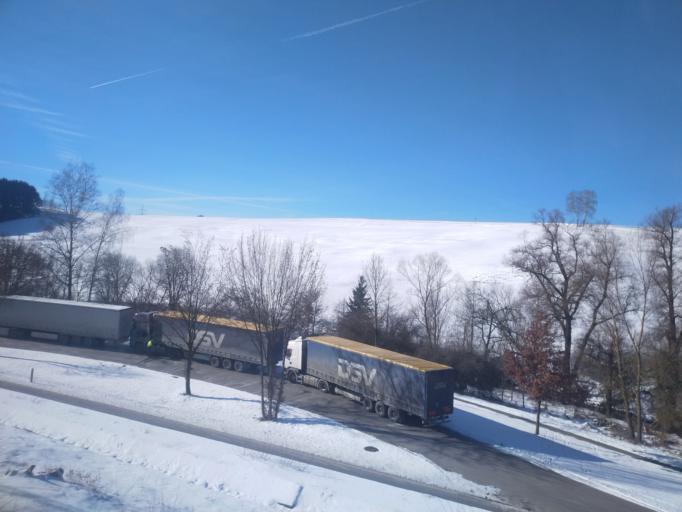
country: DE
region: Baden-Wuerttemberg
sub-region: Freiburg Region
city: Aldingen
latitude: 48.1076
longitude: 8.6966
